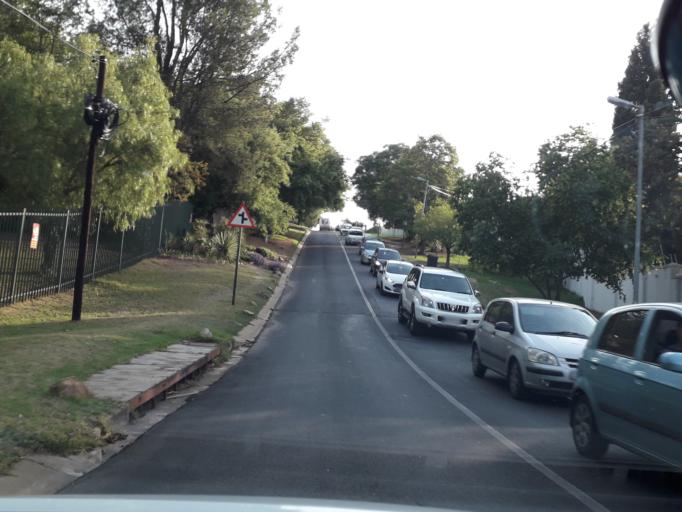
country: ZA
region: Gauteng
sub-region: City of Johannesburg Metropolitan Municipality
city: Diepsloot
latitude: -26.0663
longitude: 27.9888
